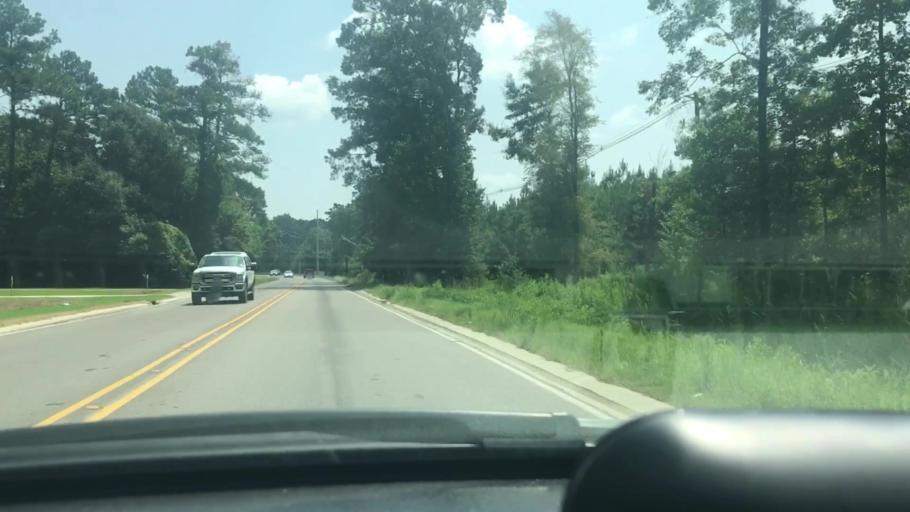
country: US
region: Louisiana
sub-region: Livingston Parish
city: Denham Springs
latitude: 30.4828
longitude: -90.9248
